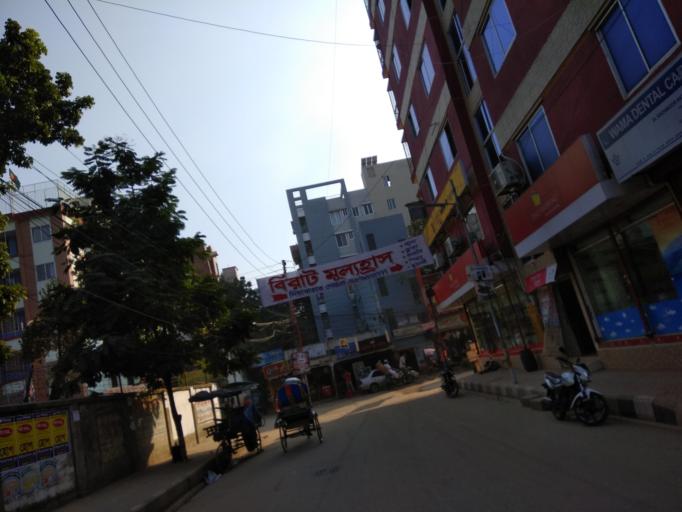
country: BD
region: Dhaka
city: Tungi
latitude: 23.8248
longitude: 90.3620
